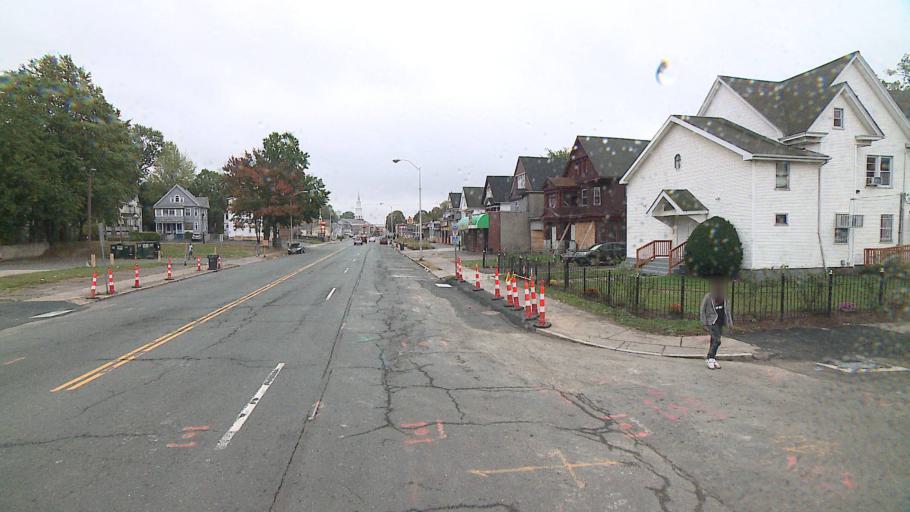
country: US
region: Connecticut
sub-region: Hartford County
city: Hartford
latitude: 41.7814
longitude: -72.6943
